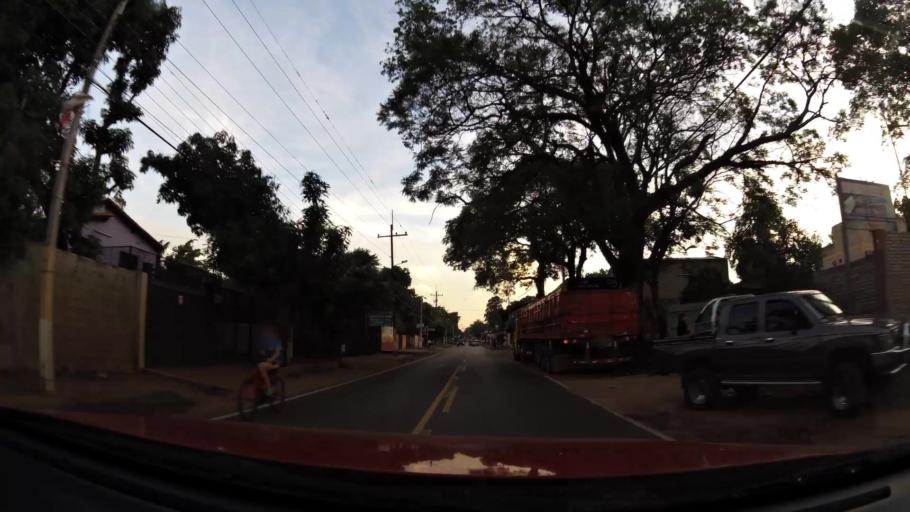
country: PY
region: Central
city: San Lorenzo
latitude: -25.3625
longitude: -57.4902
